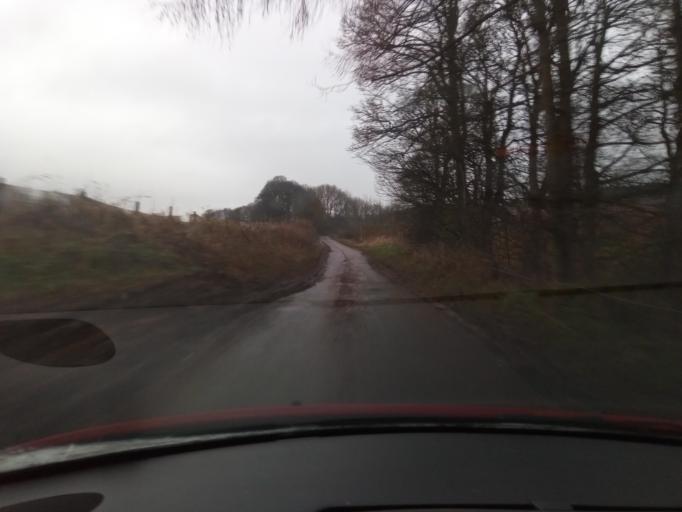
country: GB
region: Scotland
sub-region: The Scottish Borders
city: Kelso
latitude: 55.5436
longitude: -2.4365
